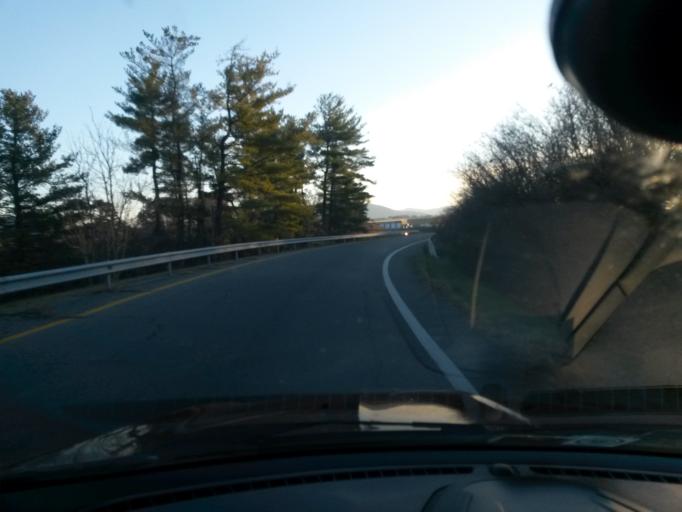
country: US
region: Virginia
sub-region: Roanoke County
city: Hollins
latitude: 37.3256
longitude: -79.9912
